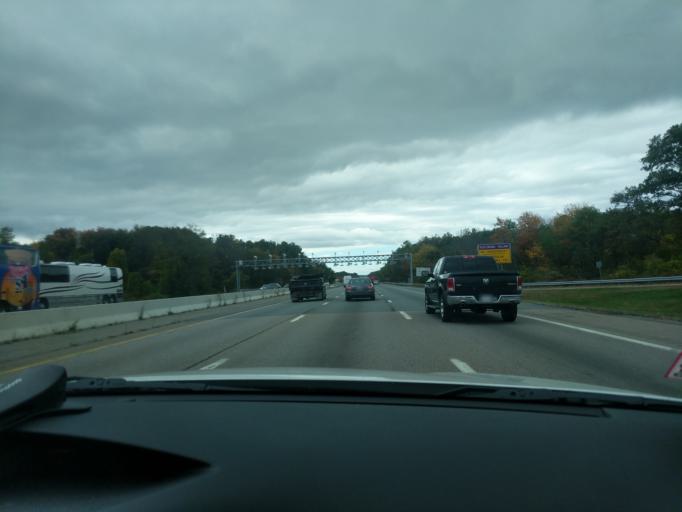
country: US
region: Massachusetts
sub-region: Worcester County
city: Cordaville
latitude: 42.2803
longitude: -71.5167
